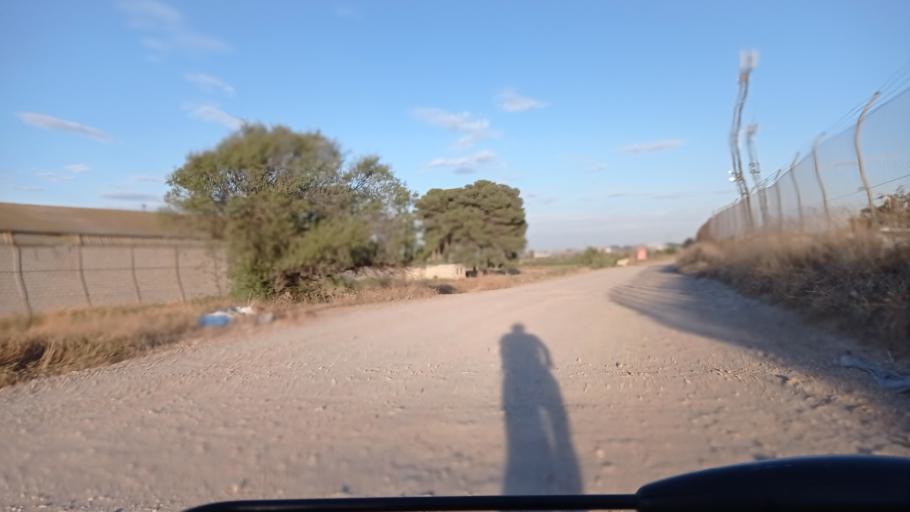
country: ES
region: Aragon
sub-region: Provincia de Zaragoza
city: Oliver-Valdefierro, Oliver, Valdefierro
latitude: 41.6757
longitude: -0.9472
